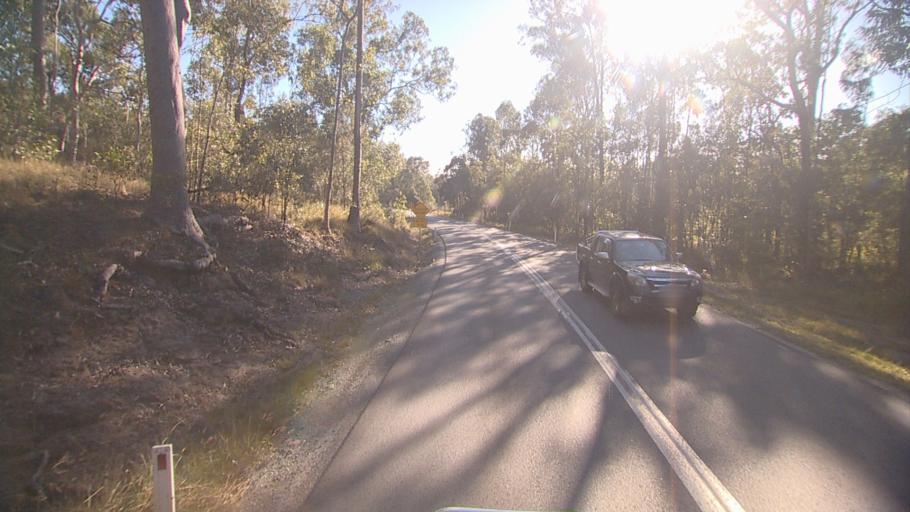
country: AU
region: Queensland
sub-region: Ipswich
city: Springfield Lakes
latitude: -27.7032
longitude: 152.9719
